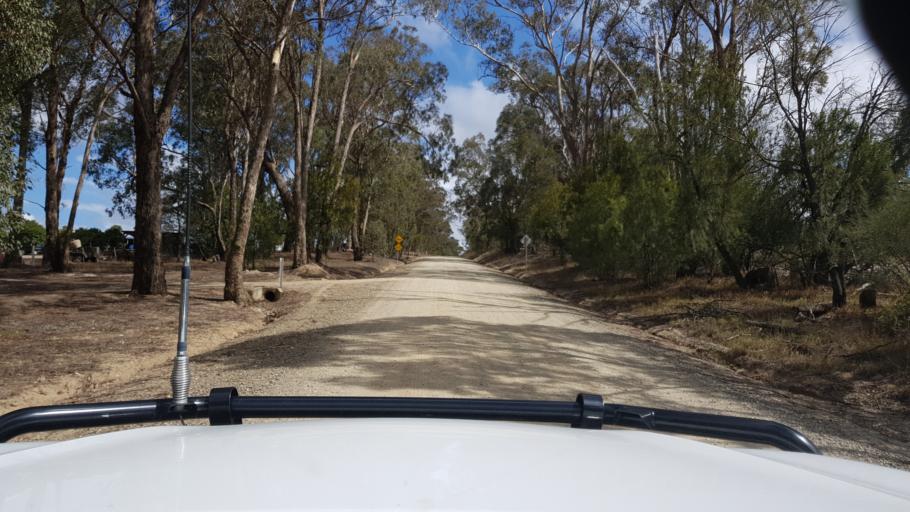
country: AU
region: Victoria
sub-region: East Gippsland
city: Bairnsdale
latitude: -37.7595
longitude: 147.6100
